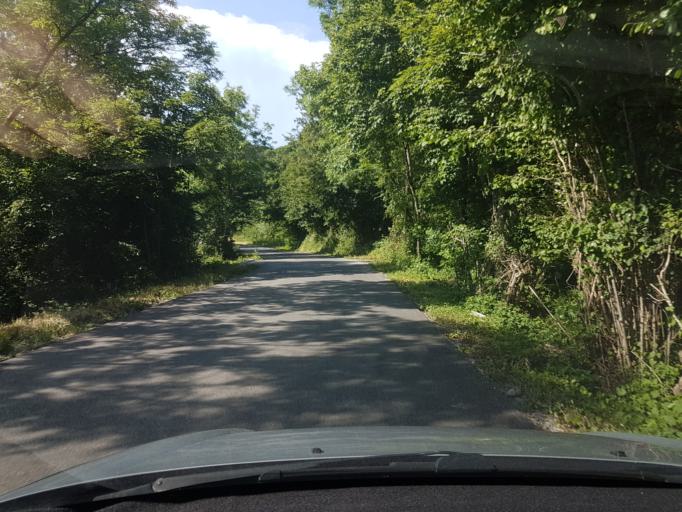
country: SI
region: Divaca
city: Divaca
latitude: 45.7366
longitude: 14.0068
